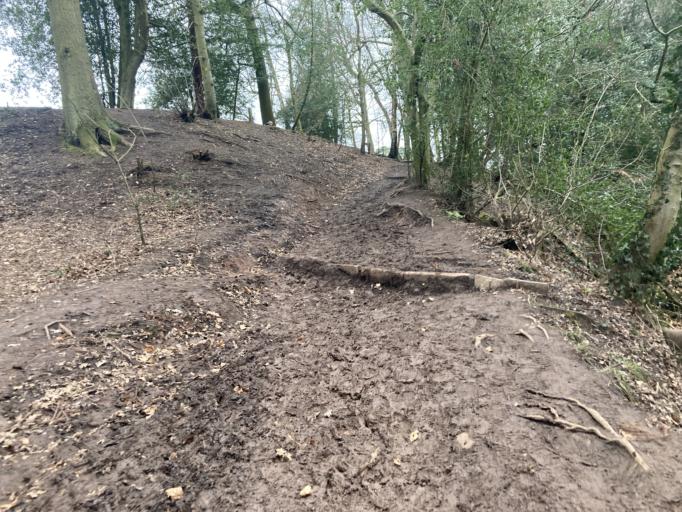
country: GB
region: England
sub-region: Cheshire East
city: Wilmslow
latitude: 53.3466
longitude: -2.2538
